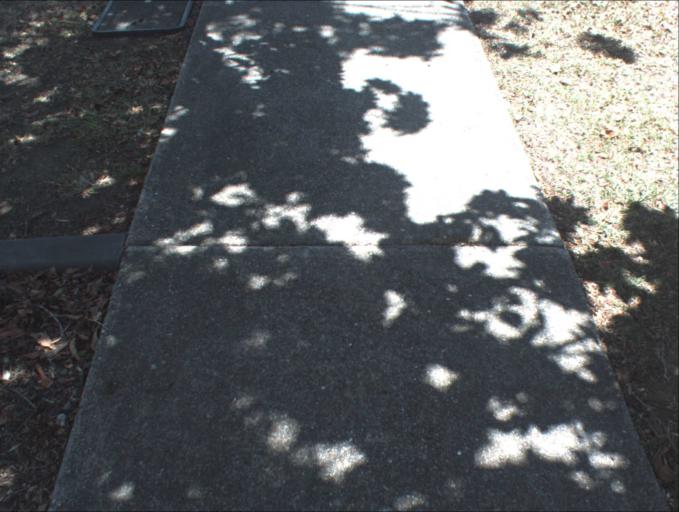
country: AU
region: Queensland
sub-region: Logan
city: Slacks Creek
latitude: -27.6424
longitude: 153.1445
